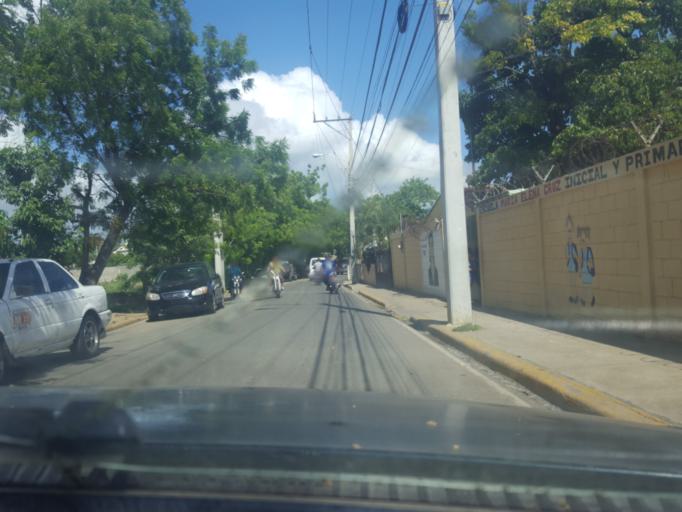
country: DO
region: Santiago
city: Santiago de los Caballeros
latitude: 19.4872
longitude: -70.7015
